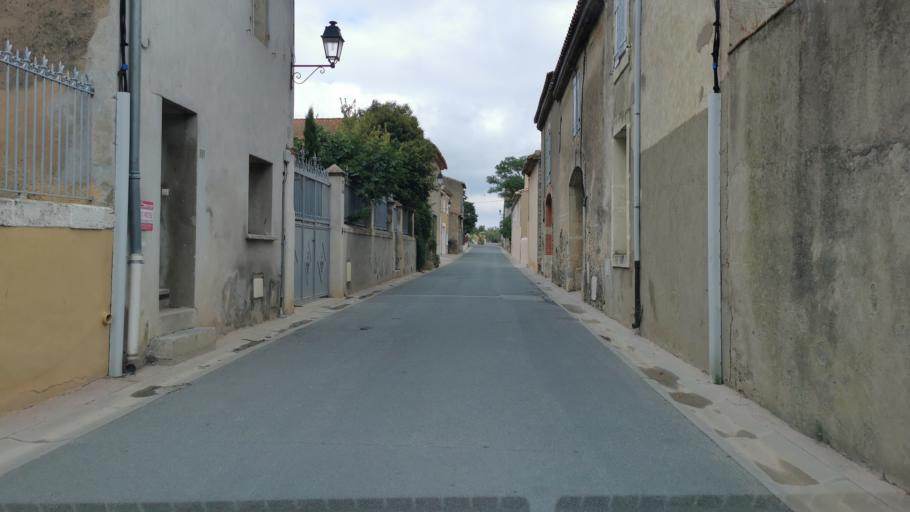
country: FR
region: Languedoc-Roussillon
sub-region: Departement de l'Aude
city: Nevian
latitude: 43.1922
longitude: 2.9278
